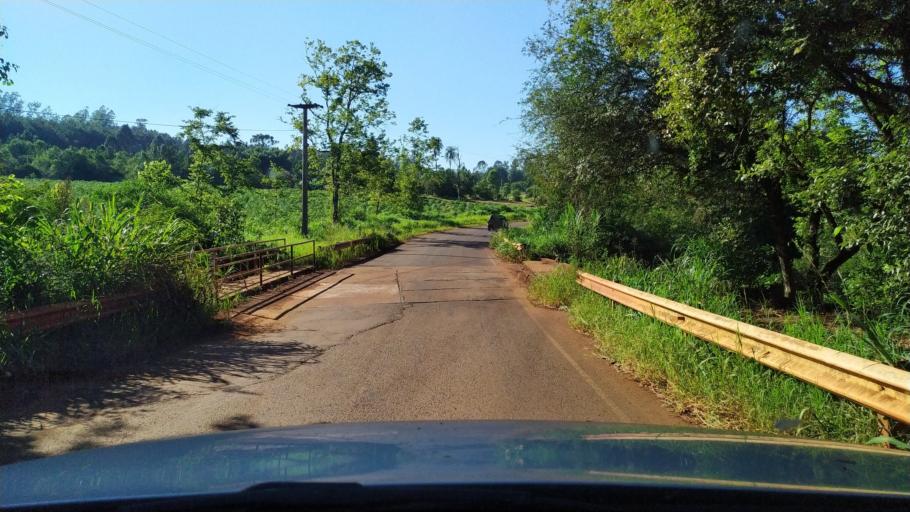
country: AR
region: Misiones
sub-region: Departamento de Montecarlo
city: Montecarlo
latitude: -26.5973
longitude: -54.7042
